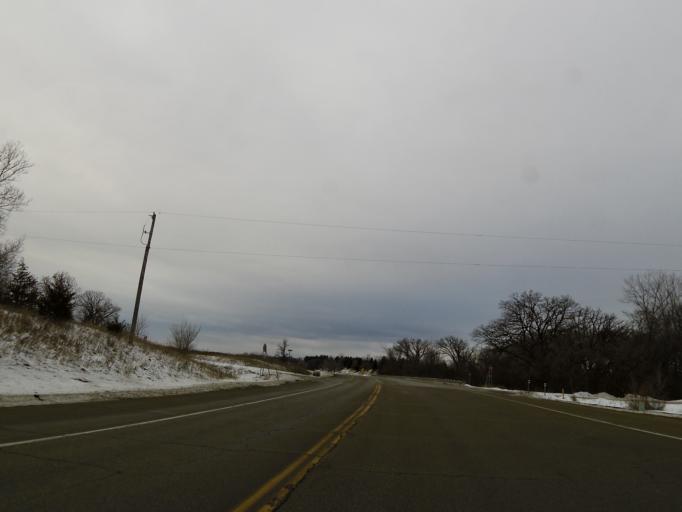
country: US
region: Wisconsin
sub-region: Saint Croix County
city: North Hudson
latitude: 44.9897
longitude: -92.7788
